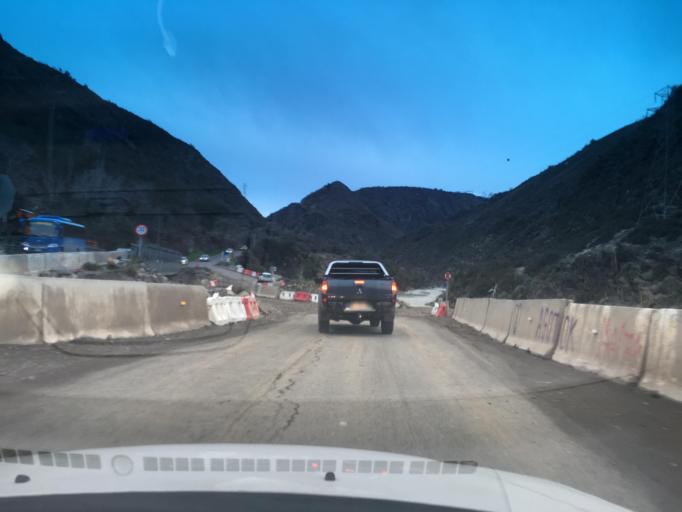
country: CL
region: Santiago Metropolitan
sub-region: Provincia de Cordillera
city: Puente Alto
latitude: -33.7338
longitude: -70.3016
